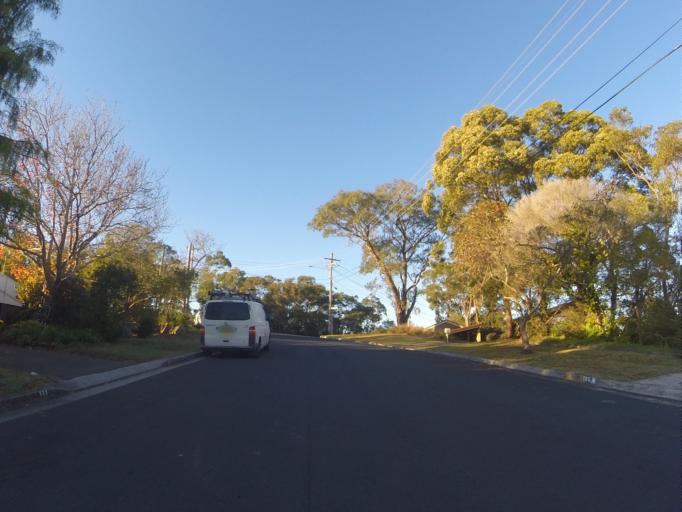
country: AU
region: New South Wales
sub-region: Sutherland Shire
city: Engadine
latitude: -34.0698
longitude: 151.0001
